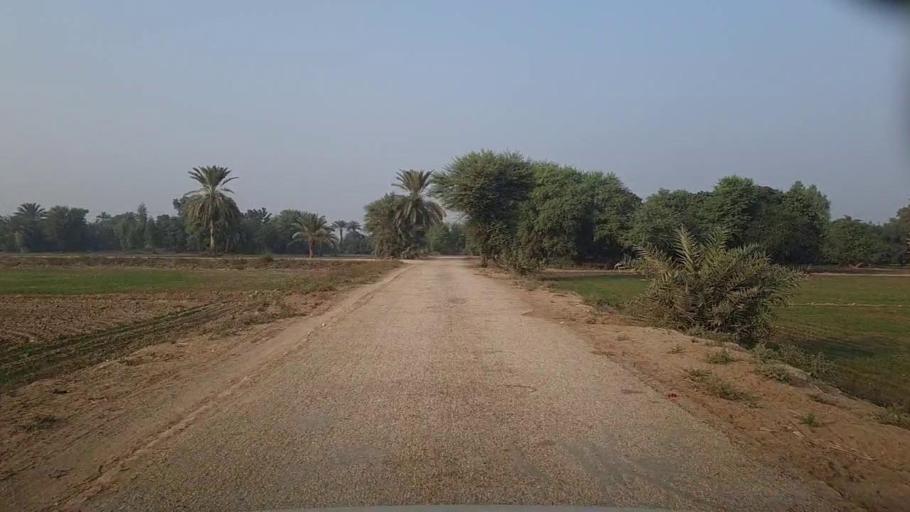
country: PK
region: Sindh
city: Kandiari
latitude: 27.0095
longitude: 68.4613
